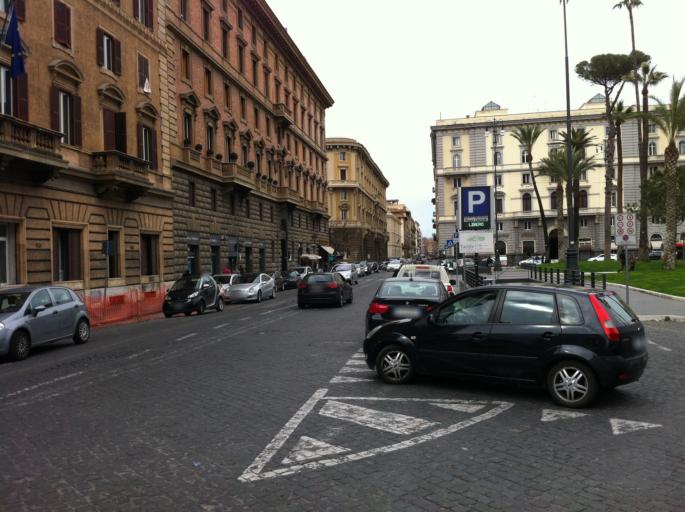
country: VA
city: Vatican City
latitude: 41.9046
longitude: 12.4690
